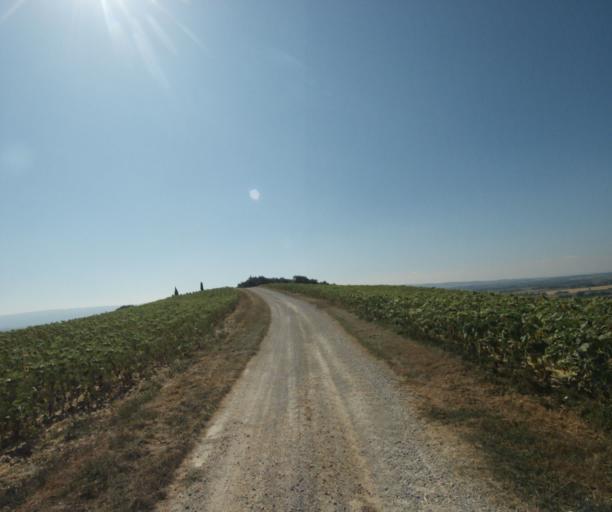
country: FR
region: Midi-Pyrenees
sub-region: Departement de la Haute-Garonne
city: Saint-Felix-Lauragais
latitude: 43.5024
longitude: 1.9354
